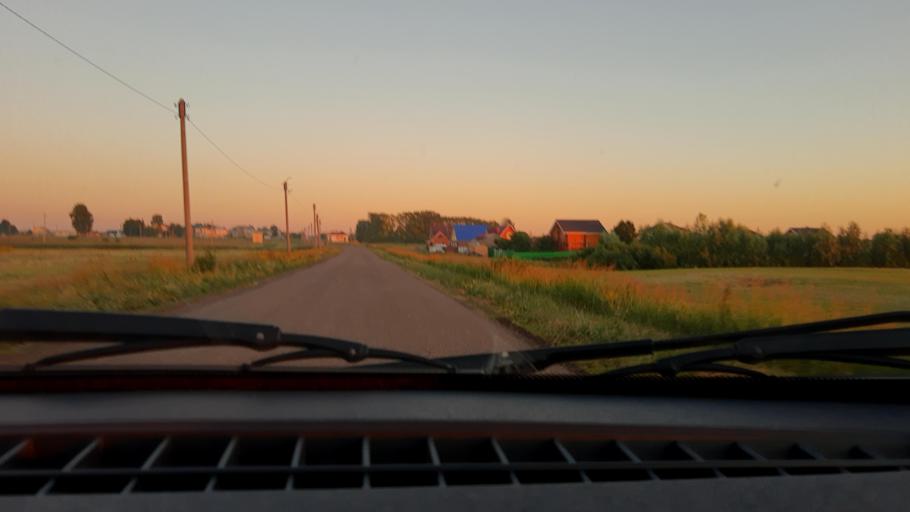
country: RU
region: Bashkortostan
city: Asanovo
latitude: 54.8948
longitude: 55.6255
